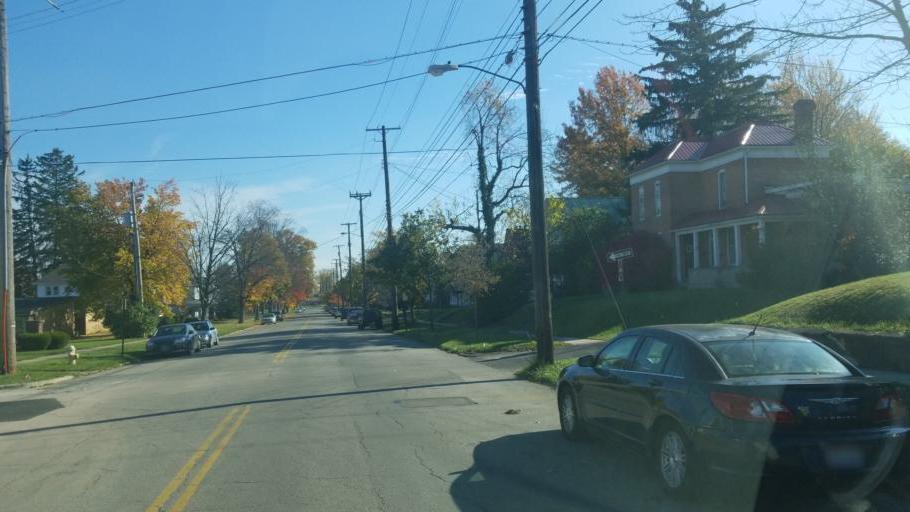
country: US
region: Ohio
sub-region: Ashland County
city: Ashland
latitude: 40.8624
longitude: -82.3178
